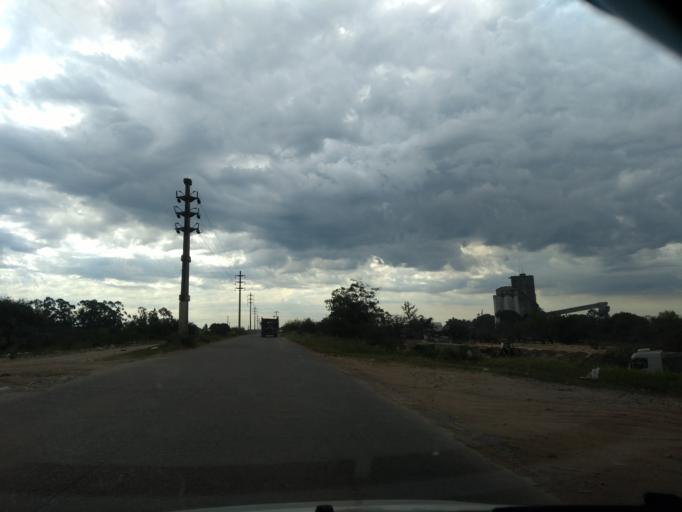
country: AR
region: Chaco
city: Barranqueras
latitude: -27.4761
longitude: -58.9152
